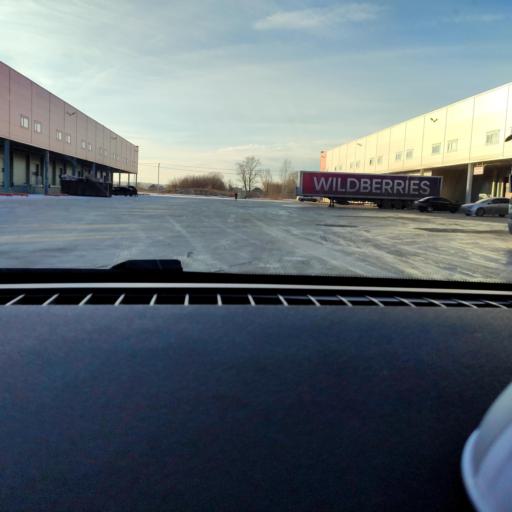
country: RU
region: Samara
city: Samara
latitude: 53.0910
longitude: 50.1275
